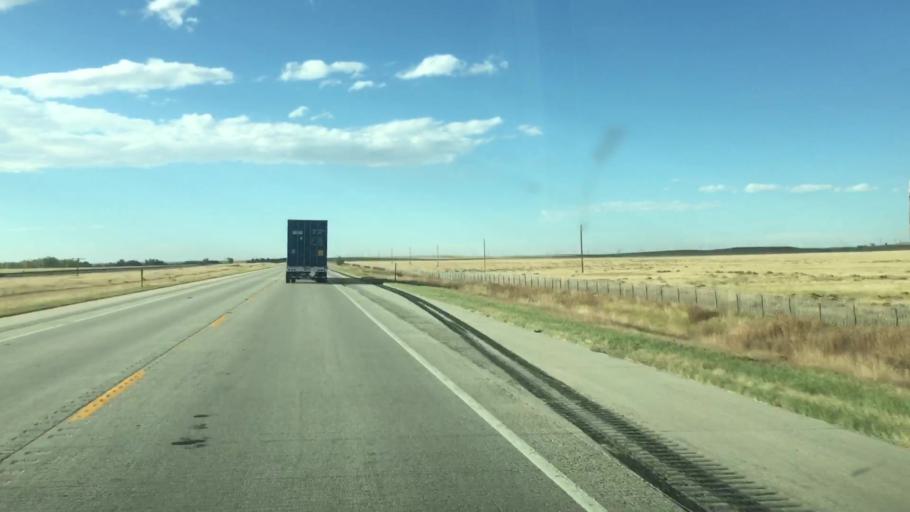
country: US
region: Colorado
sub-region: Lincoln County
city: Limon
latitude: 39.2217
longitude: -103.6080
